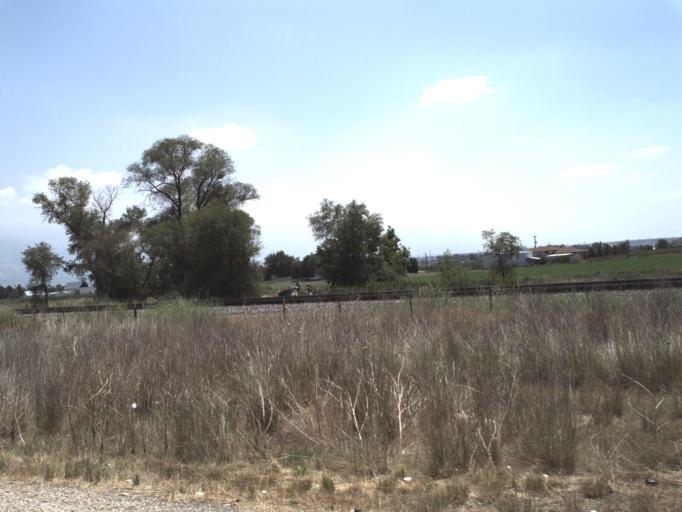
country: US
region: Utah
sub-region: Weber County
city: West Haven
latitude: 41.2444
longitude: -112.0810
